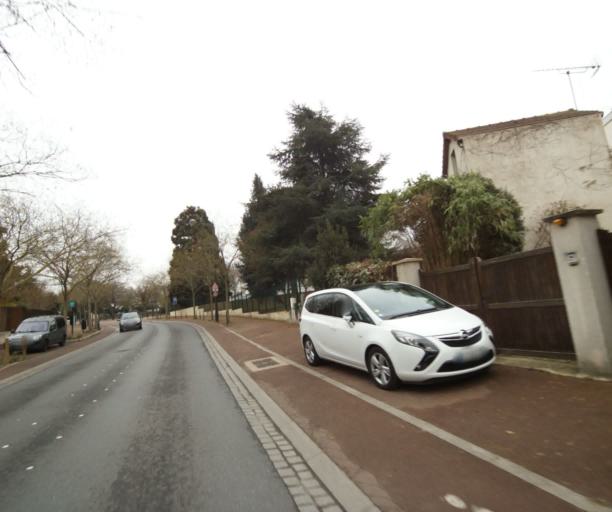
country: FR
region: Ile-de-France
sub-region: Departement des Hauts-de-Seine
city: Rueil-Malmaison
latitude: 48.8655
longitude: 2.1872
